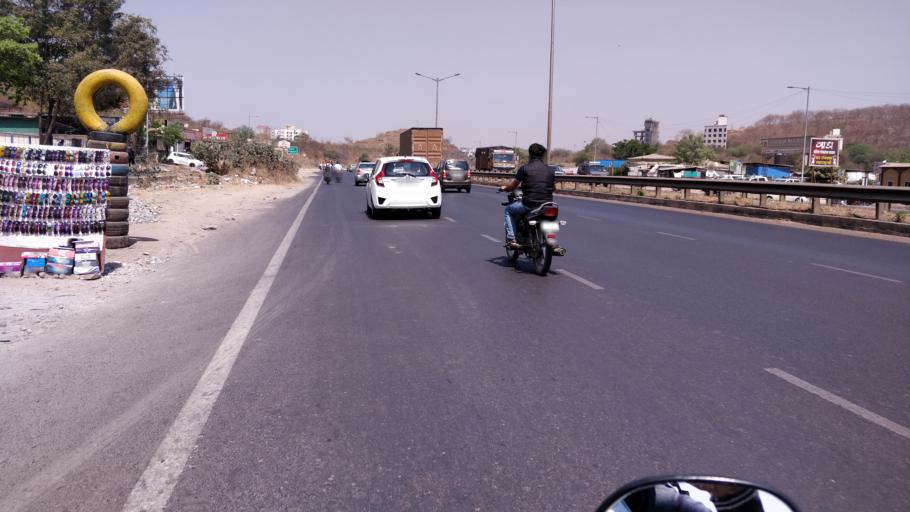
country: IN
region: Maharashtra
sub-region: Pune Division
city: Shivaji Nagar
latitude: 18.5430
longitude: 73.7764
